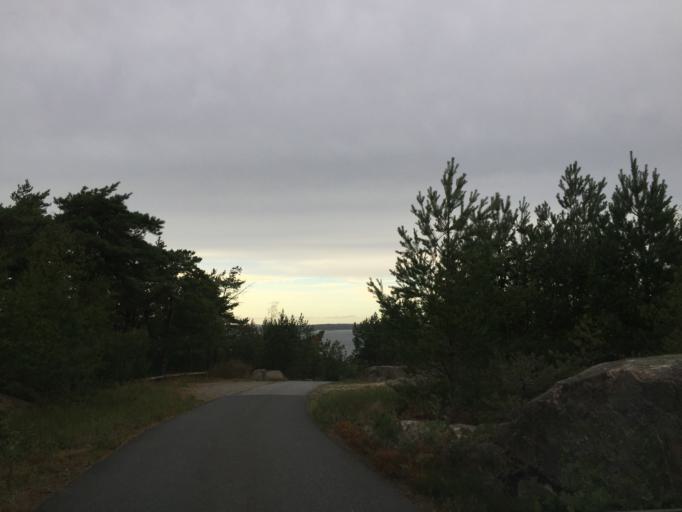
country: NO
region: Ostfold
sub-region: Hvaler
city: Skjaerhalden
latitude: 59.0816
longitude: 11.0002
